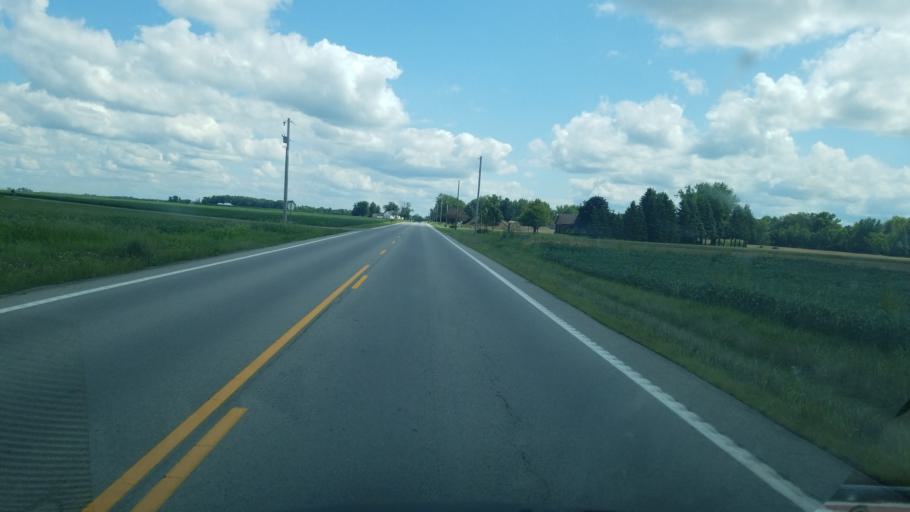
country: US
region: Ohio
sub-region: Putnam County
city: Kalida
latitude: 40.9529
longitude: -84.1691
